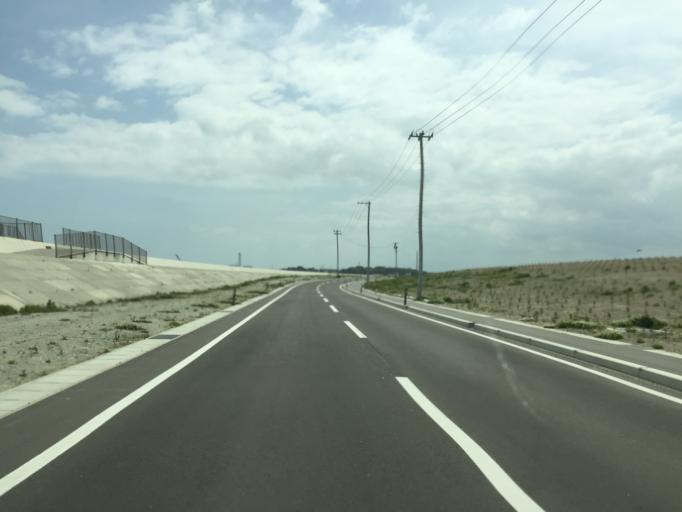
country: JP
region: Miyagi
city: Marumori
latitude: 37.8837
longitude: 140.9324
